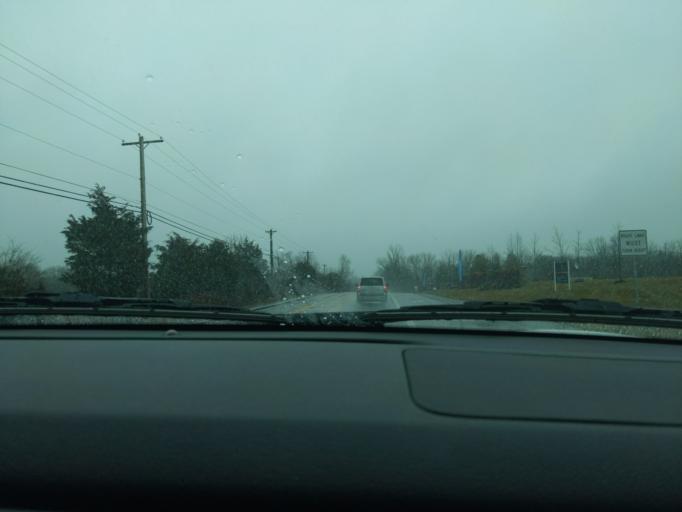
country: US
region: Pennsylvania
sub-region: Bucks County
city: Dublin
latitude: 40.3864
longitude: -75.2262
